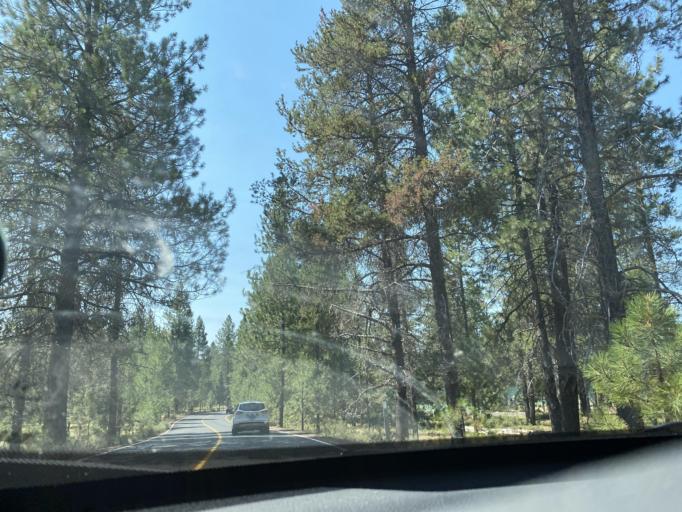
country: US
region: Oregon
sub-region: Deschutes County
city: Sunriver
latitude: 43.8902
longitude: -121.4283
